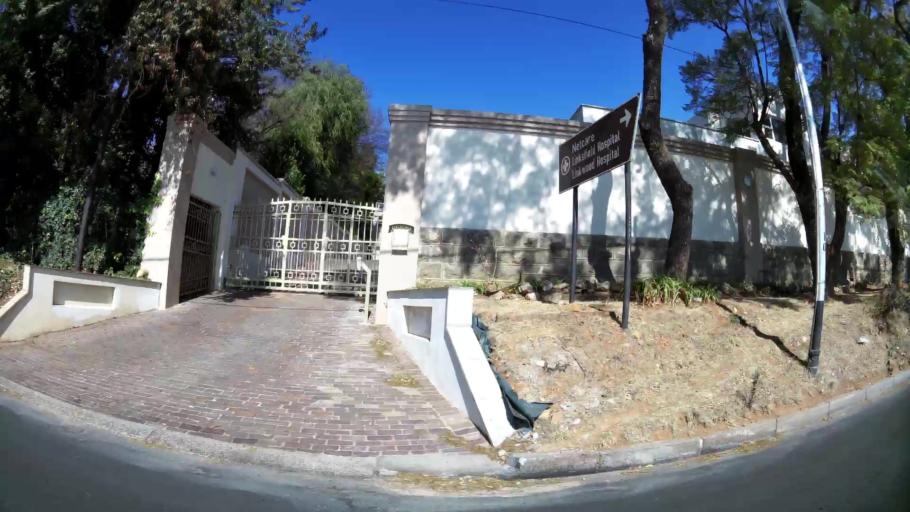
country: ZA
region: Gauteng
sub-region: City of Johannesburg Metropolitan Municipality
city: Johannesburg
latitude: -26.1647
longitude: 28.0950
